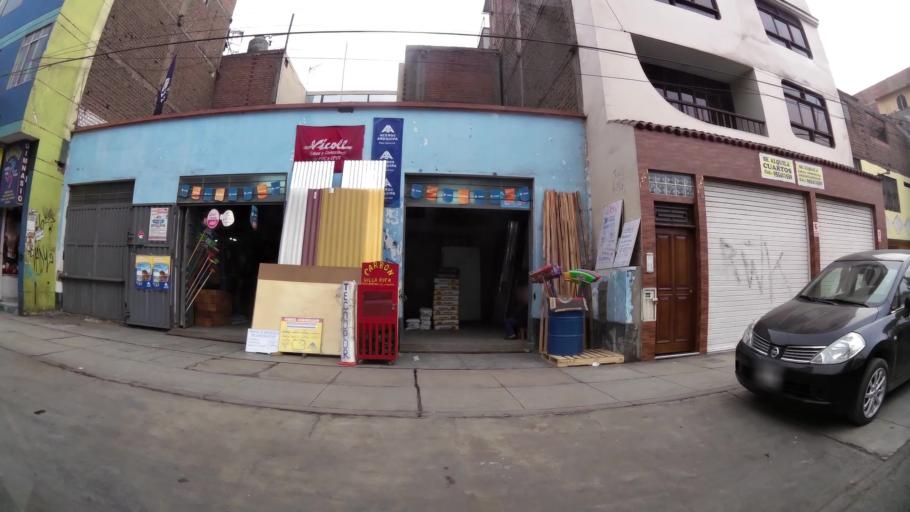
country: PE
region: Lima
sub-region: Lima
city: Independencia
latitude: -12.0036
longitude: -77.0026
